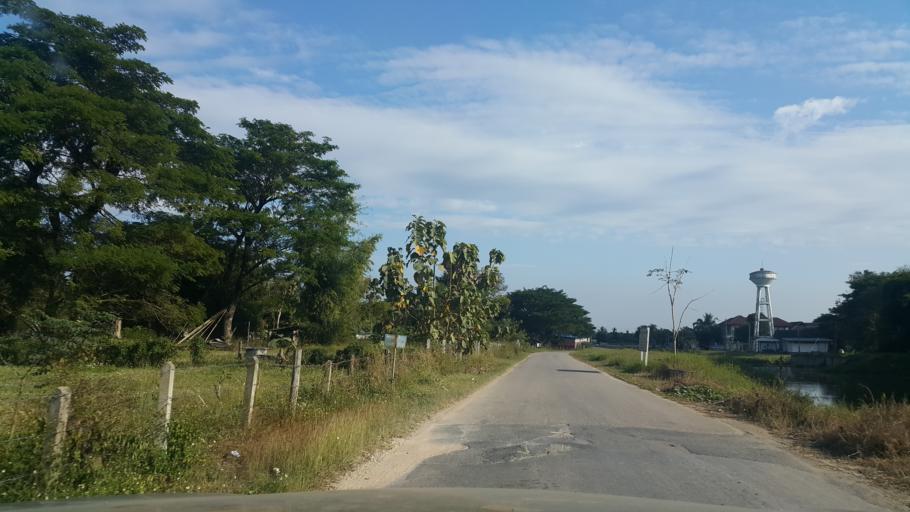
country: TH
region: Lampang
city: Hang Chat
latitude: 18.3159
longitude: 99.3486
